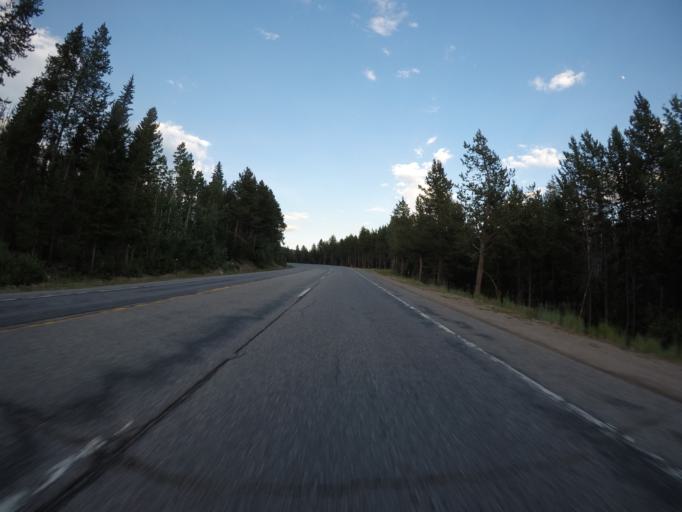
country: US
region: Colorado
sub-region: Routt County
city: Steamboat Springs
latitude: 40.3489
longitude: -106.7472
